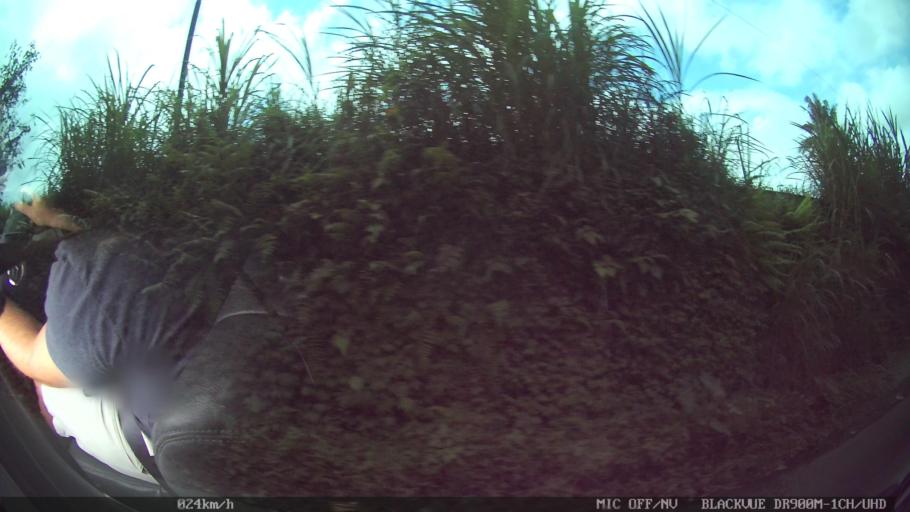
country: ID
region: Bali
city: Banjar Petak
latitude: -8.4443
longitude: 115.3226
